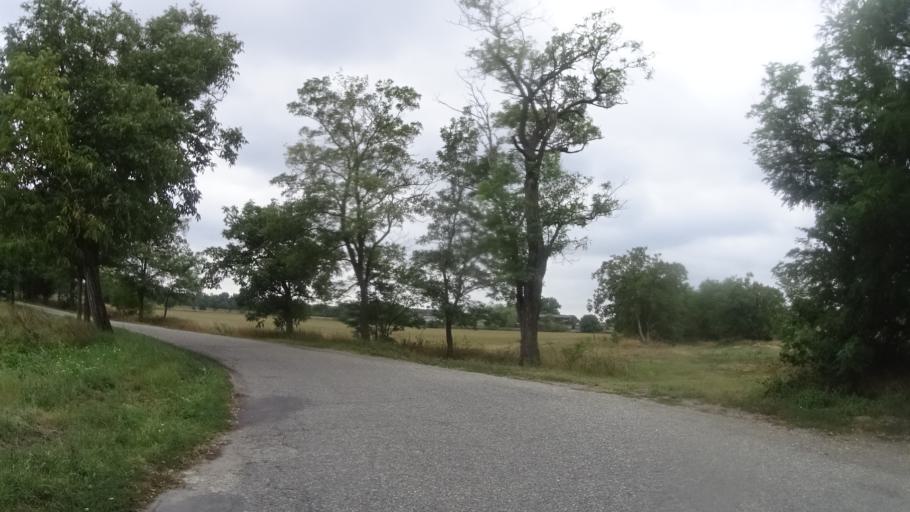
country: HU
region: Komarom-Esztergom
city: Acs
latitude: 47.7624
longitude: 17.9514
